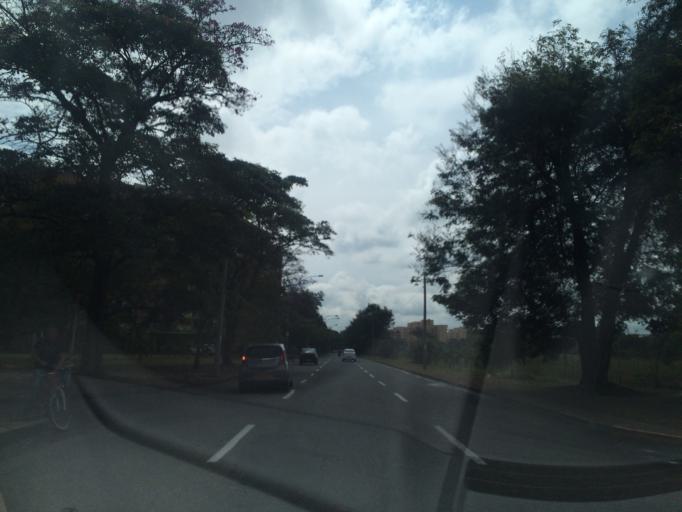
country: CO
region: Valle del Cauca
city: Cali
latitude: 3.3798
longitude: -76.5325
